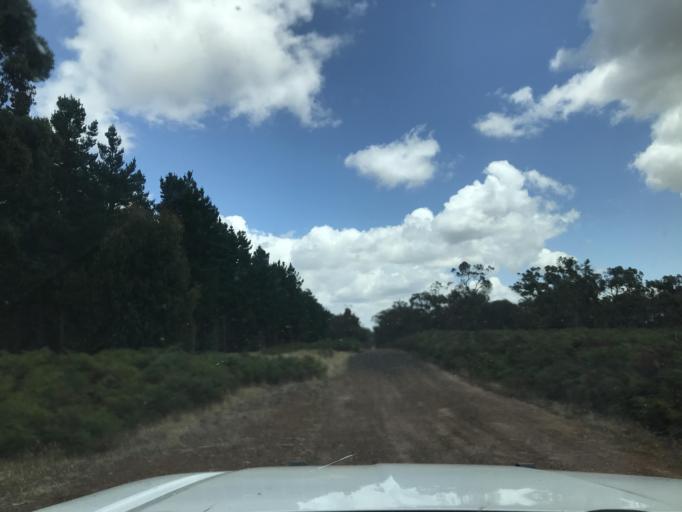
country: AU
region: South Australia
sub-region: Wattle Range
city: Penola
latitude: -37.0755
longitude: 141.3436
